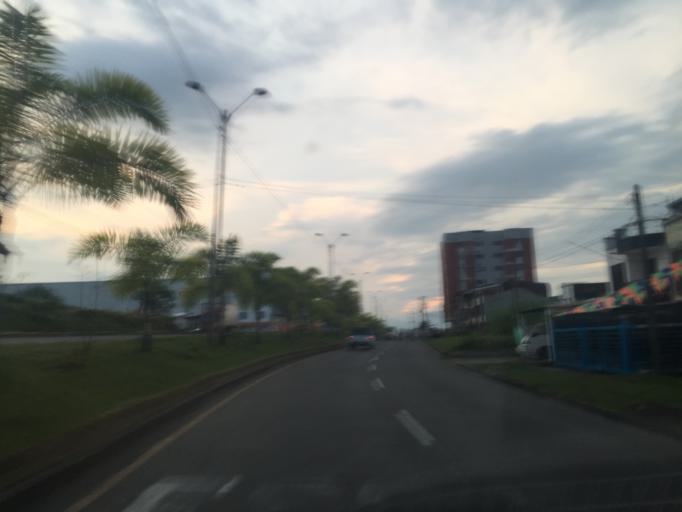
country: CO
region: Risaralda
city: Pereira
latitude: 4.7997
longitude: -75.7463
